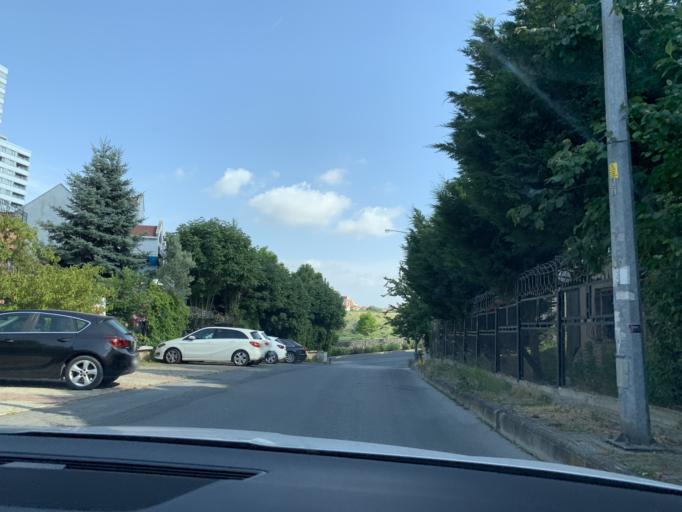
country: TR
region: Istanbul
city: Esenyurt
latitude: 41.0786
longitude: 28.6737
